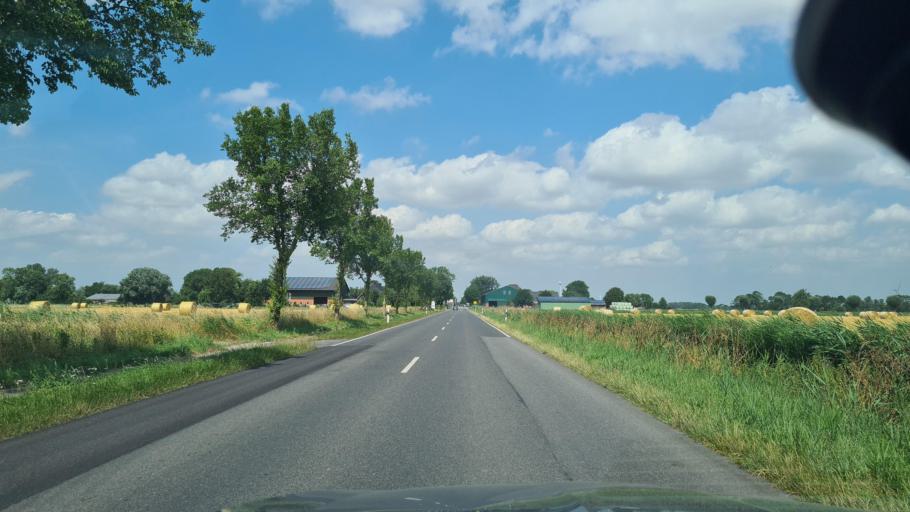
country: DE
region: Schleswig-Holstein
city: Wohrden
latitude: 54.1405
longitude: 9.0166
